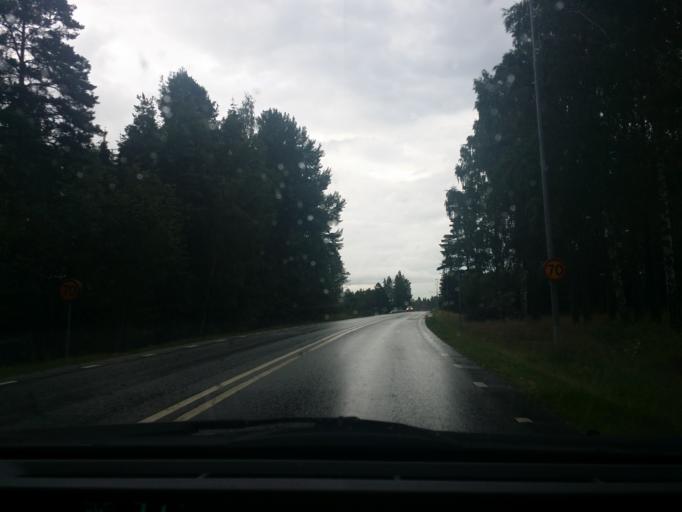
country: SE
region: OErebro
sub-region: Lindesbergs Kommun
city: Frovi
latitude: 59.4746
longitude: 15.3708
